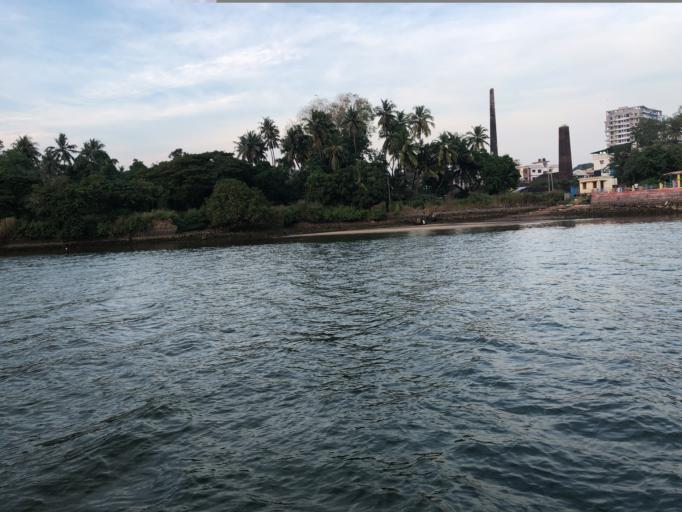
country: IN
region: Karnataka
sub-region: Dakshina Kannada
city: Ullal
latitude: 12.8427
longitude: 74.8415
